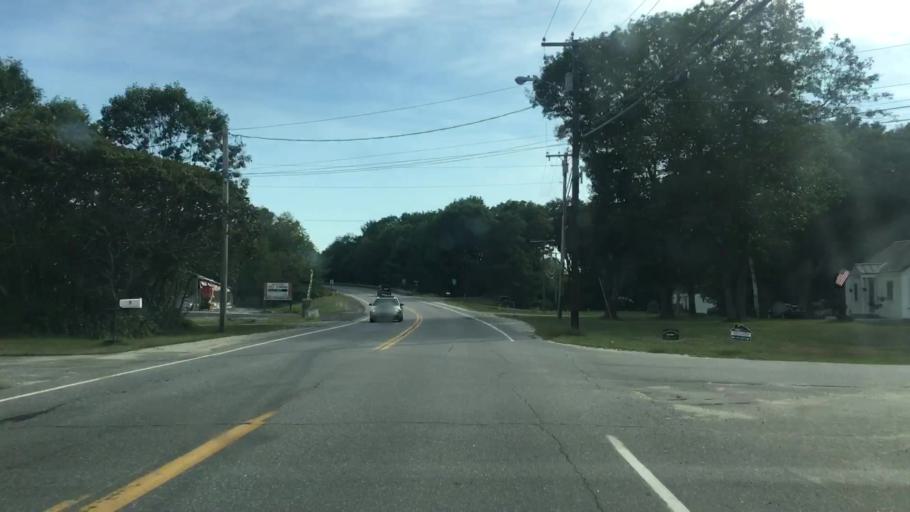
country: US
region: Maine
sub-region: Cumberland County
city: Brunswick
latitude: 43.9151
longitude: -69.9061
